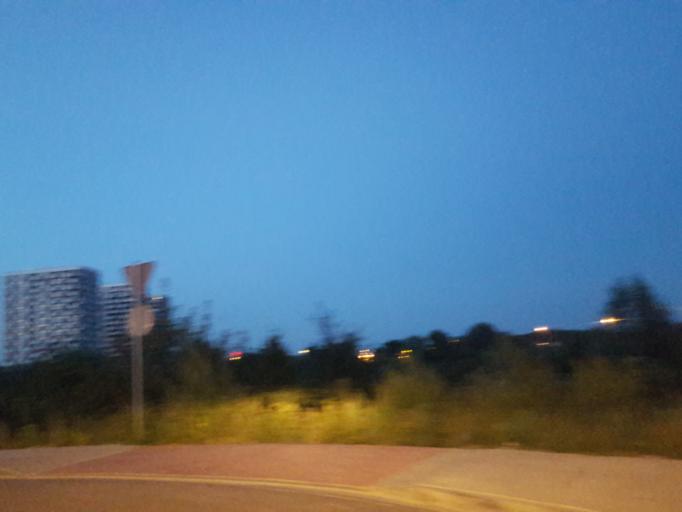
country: PL
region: Masovian Voivodeship
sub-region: Warszawa
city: Praga Poludnie
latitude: 52.2284
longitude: 21.1105
